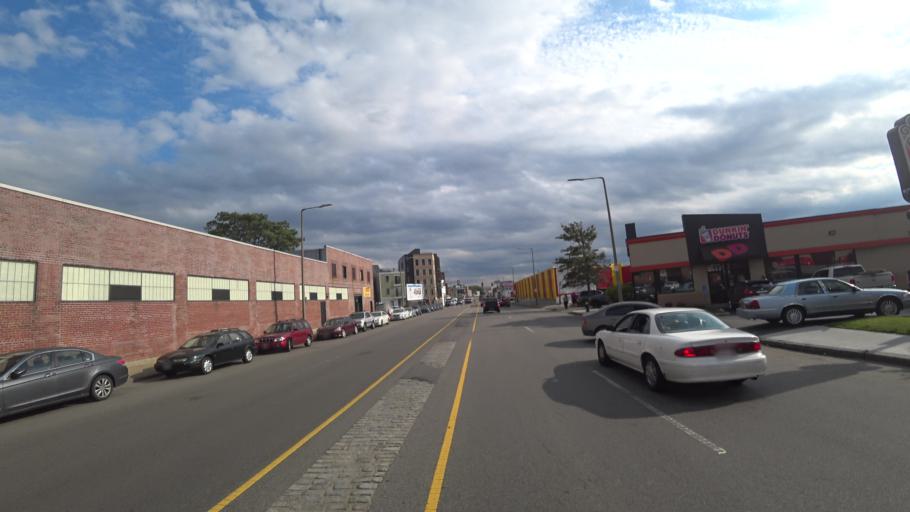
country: US
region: Massachusetts
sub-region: Suffolk County
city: South Boston
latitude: 42.3361
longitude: -71.0559
